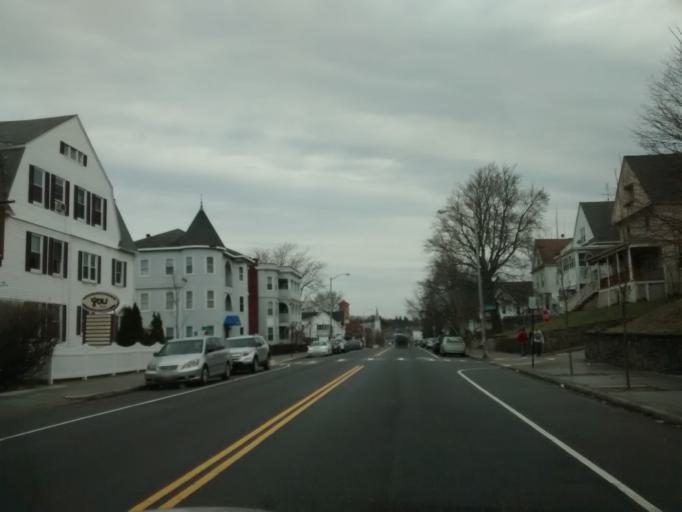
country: US
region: Massachusetts
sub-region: Worcester County
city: Worcester
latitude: 42.2800
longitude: -71.7933
